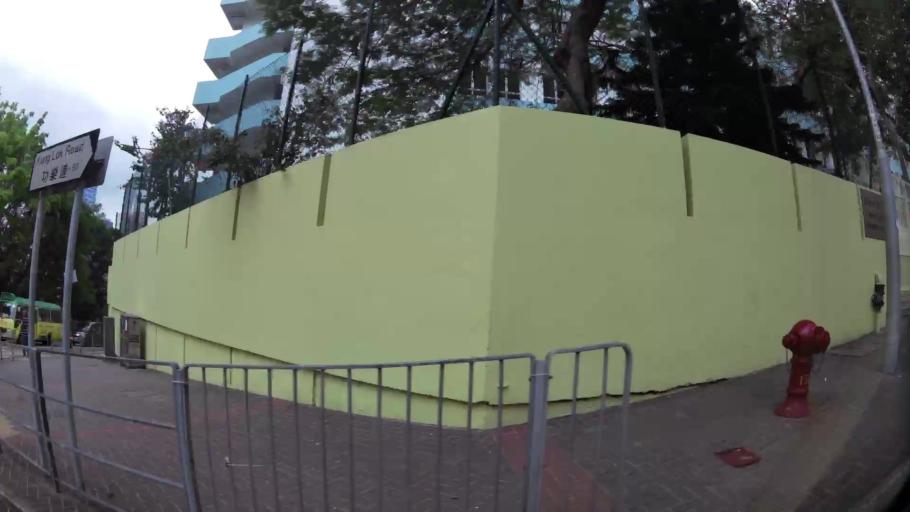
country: HK
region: Kowloon City
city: Kowloon
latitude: 22.3183
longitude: 114.2225
